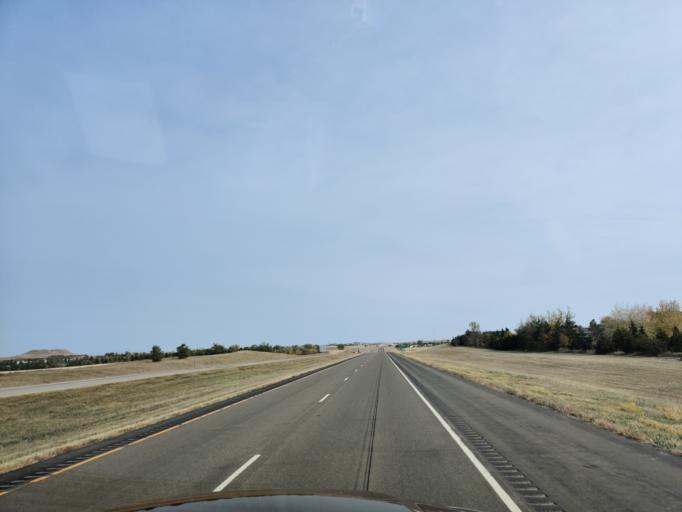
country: US
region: North Dakota
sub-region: Stark County
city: Dickinson
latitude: 46.8944
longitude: -102.7681
